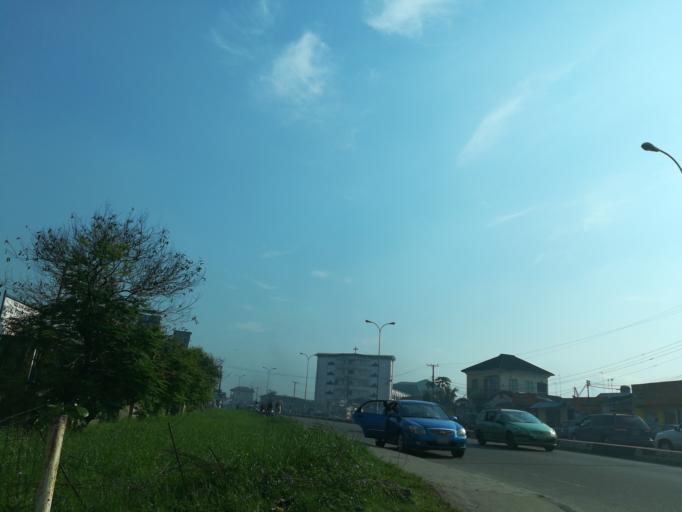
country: NG
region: Rivers
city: Port Harcourt
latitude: 4.8135
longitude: 7.0210
